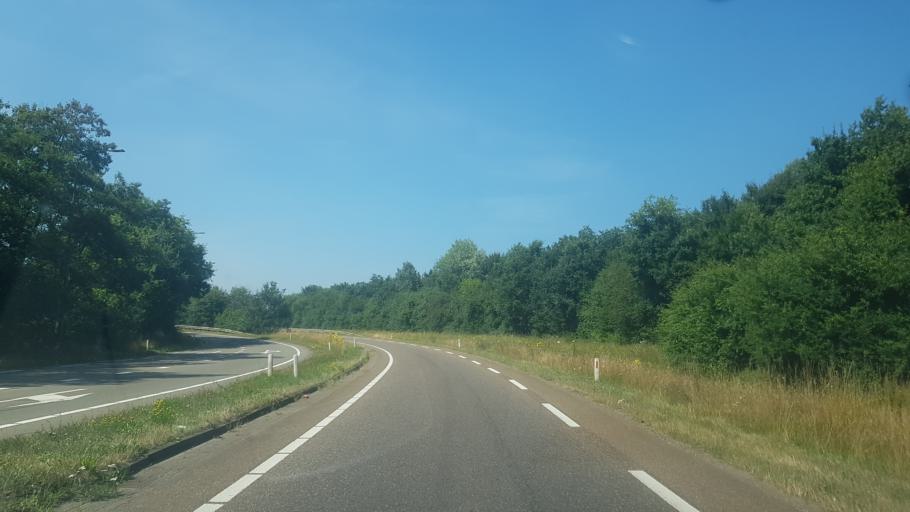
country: NL
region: North Brabant
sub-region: Gemeente Helmond
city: Helmond
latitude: 51.4712
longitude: 5.7192
